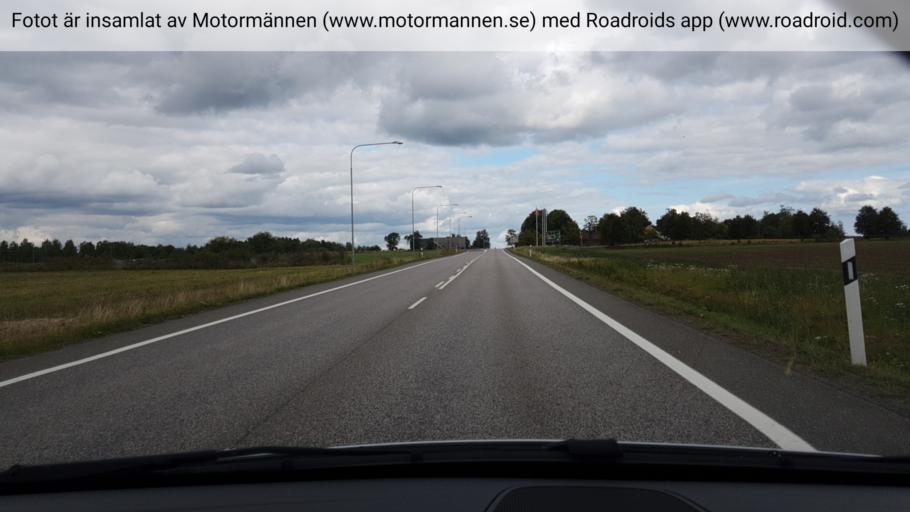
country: SE
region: Vaestra Goetaland
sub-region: Tidaholms Kommun
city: Tidaholm
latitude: 58.1628
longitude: 13.9354
